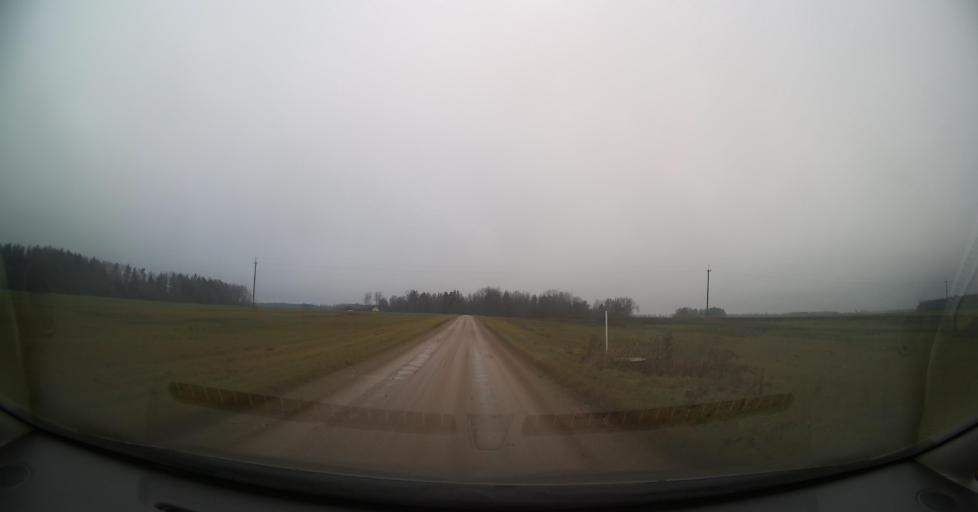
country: EE
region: Tartu
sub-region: Tartu linn
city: Tartu
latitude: 58.3752
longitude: 26.9309
